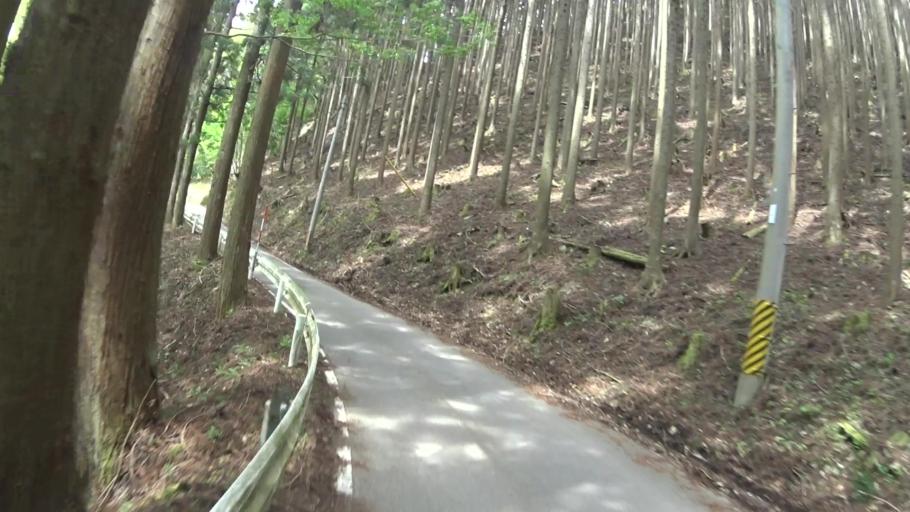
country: JP
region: Kyoto
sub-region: Kyoto-shi
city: Kamigyo-ku
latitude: 35.1718
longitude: 135.7432
